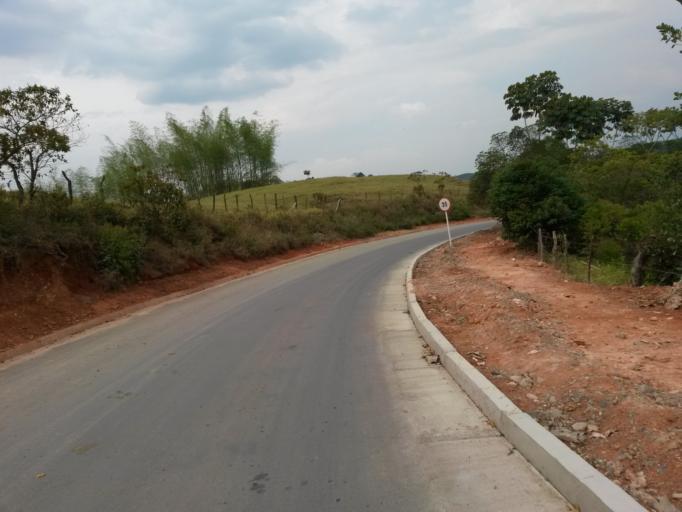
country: CO
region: Cauca
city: Buenos Aires
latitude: 3.0881
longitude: -76.6058
